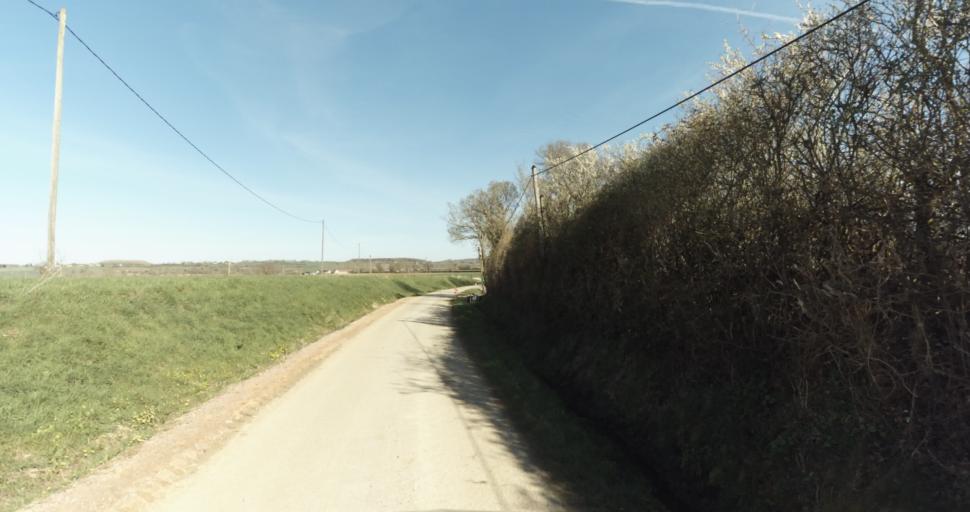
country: FR
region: Lower Normandy
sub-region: Departement du Calvados
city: Saint-Pierre-sur-Dives
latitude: 49.0369
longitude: -0.0003
